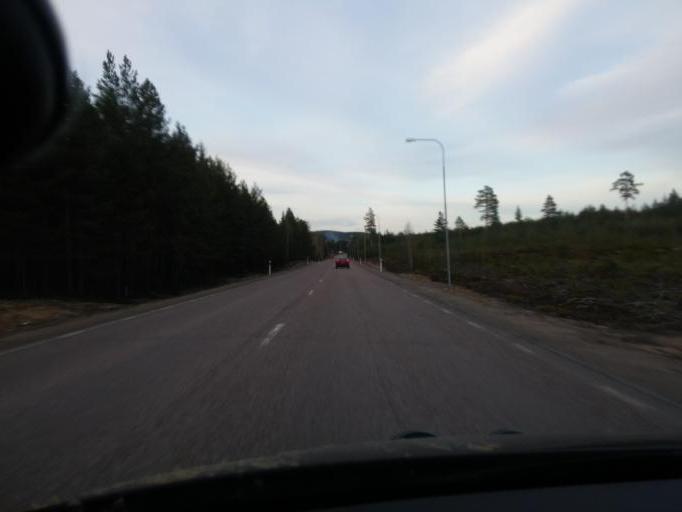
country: SE
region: Gaevleborg
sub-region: Ljusdals Kommun
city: Ljusdal
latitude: 61.8359
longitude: 16.0296
